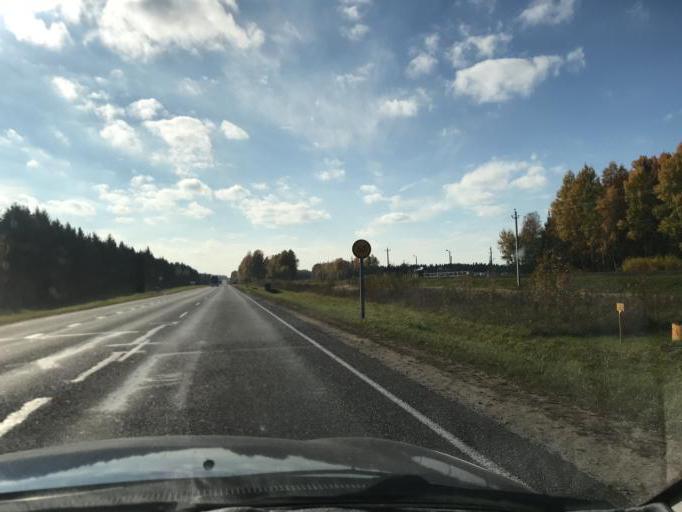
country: BY
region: Grodnenskaya
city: Voranava
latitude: 54.2104
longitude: 25.3513
